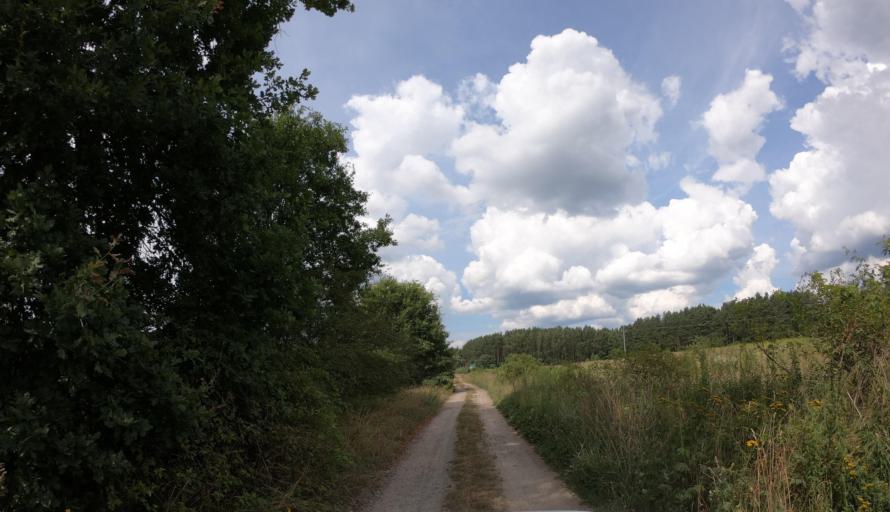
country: PL
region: West Pomeranian Voivodeship
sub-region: Powiat stargardzki
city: Kobylanka
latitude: 53.3254
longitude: 14.8220
